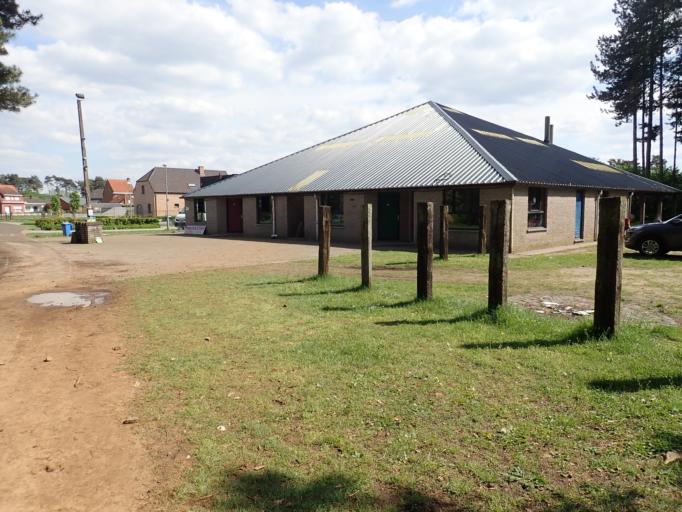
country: BE
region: Flanders
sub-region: Provincie Antwerpen
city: Lille
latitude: 51.2416
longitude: 4.8158
